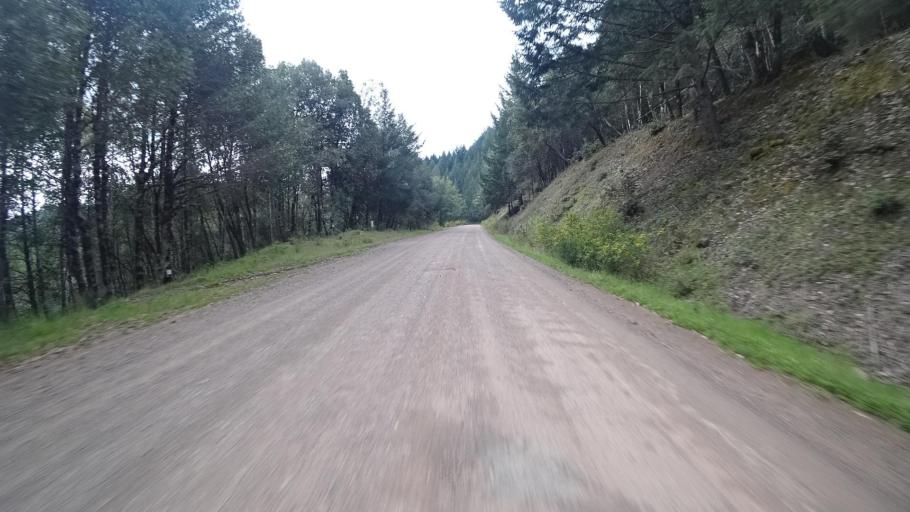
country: US
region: California
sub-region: Humboldt County
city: Redway
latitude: 40.2256
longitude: -123.7613
